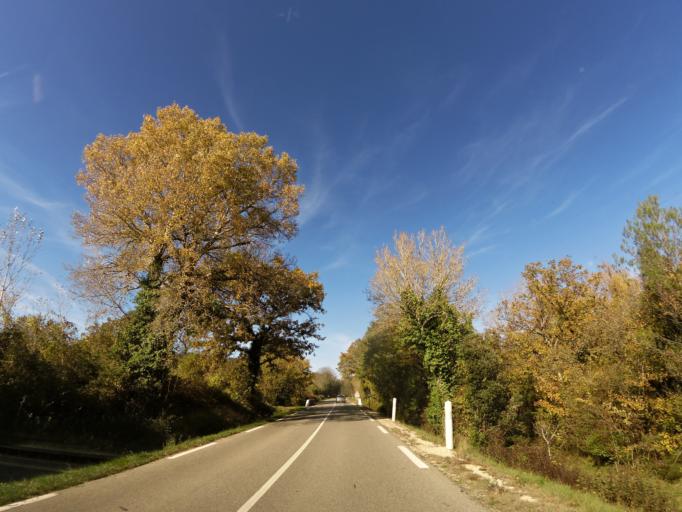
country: FR
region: Languedoc-Roussillon
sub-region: Departement du Gard
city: Ledignan
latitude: 43.9217
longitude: 4.1060
